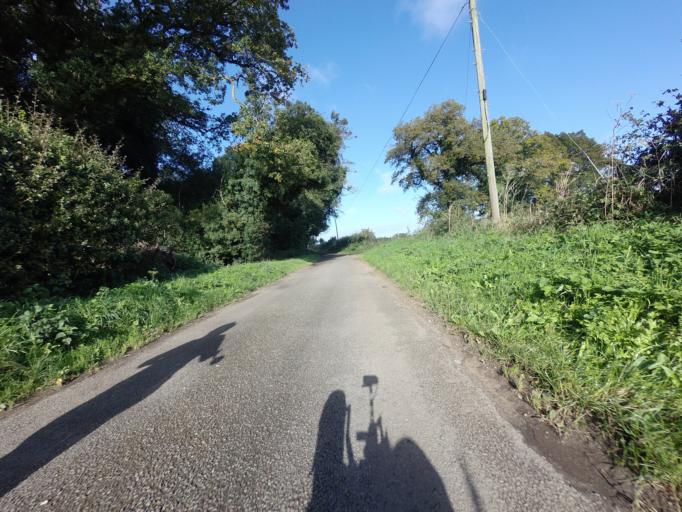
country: GB
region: England
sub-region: Norfolk
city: Dersingham
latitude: 52.8505
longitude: 0.6707
